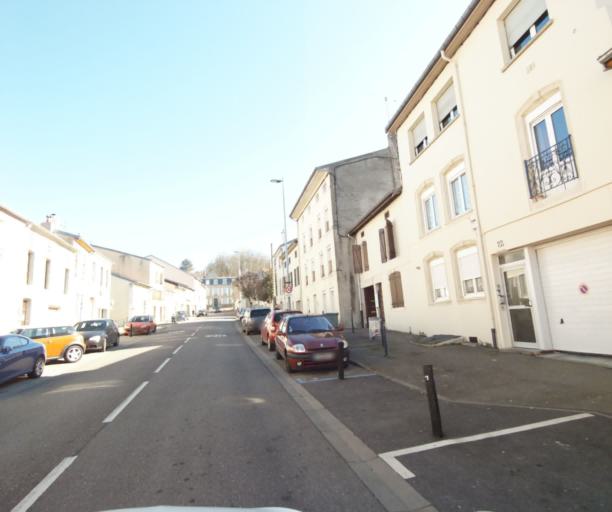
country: FR
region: Lorraine
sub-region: Departement de Meurthe-et-Moselle
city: Malzeville
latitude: 48.7093
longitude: 6.1857
